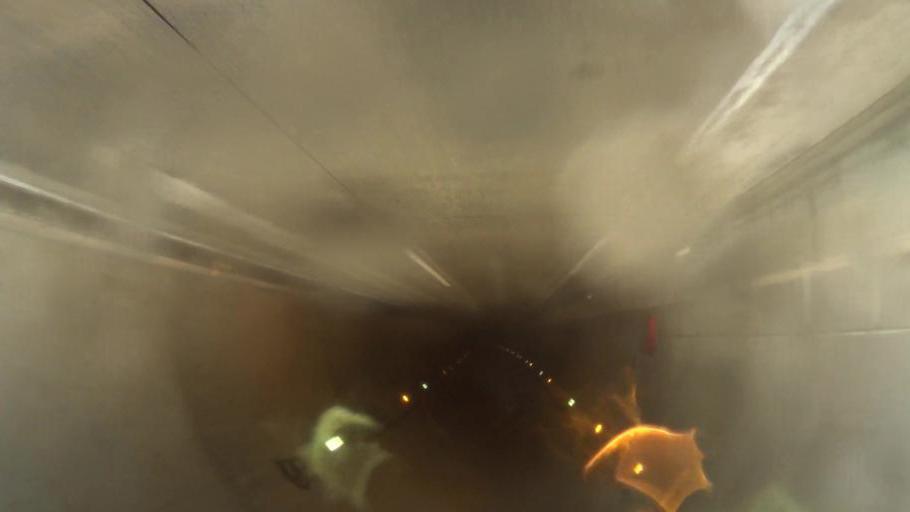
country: JP
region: Kyoto
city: Kameoka
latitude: 35.0672
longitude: 135.5231
